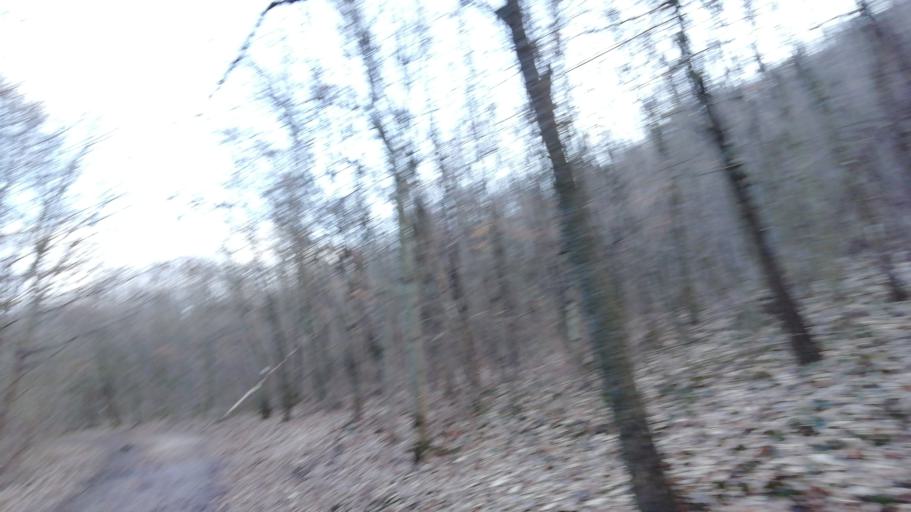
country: HU
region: Pest
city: Budakeszi
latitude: 47.5354
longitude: 18.9570
